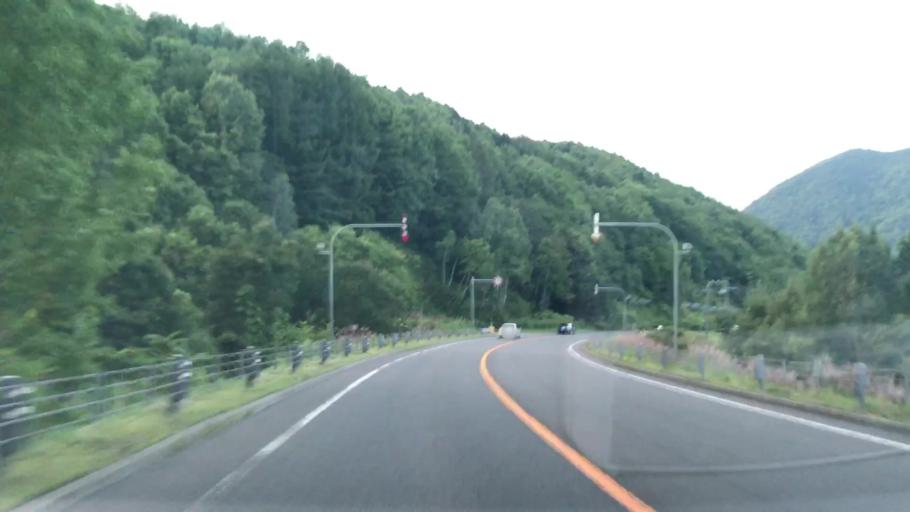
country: JP
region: Hokkaido
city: Sapporo
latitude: 42.9105
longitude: 141.1199
